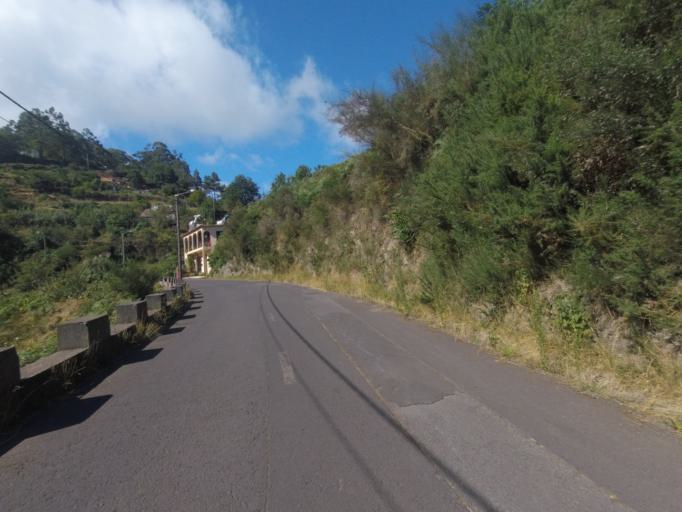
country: PT
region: Madeira
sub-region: Ribeira Brava
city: Campanario
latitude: 32.6964
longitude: -17.0178
